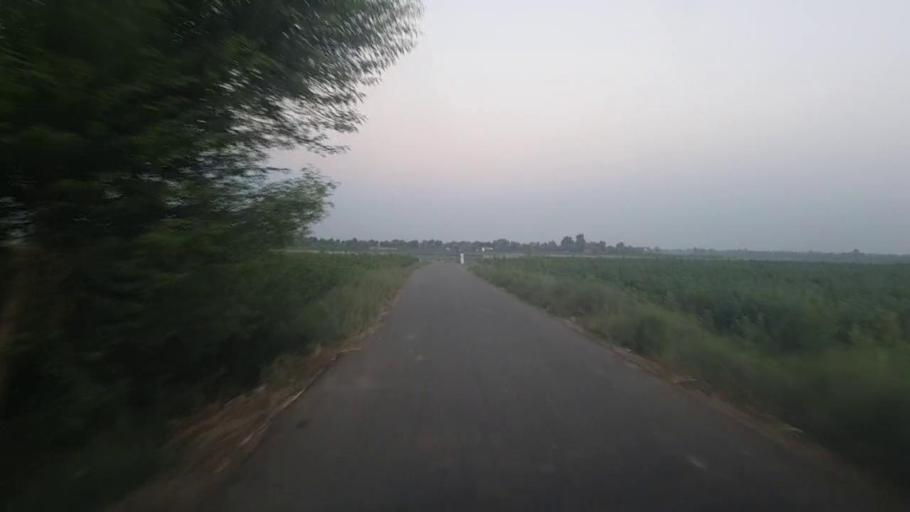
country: PK
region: Sindh
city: Ubauro
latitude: 28.1072
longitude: 69.7725
